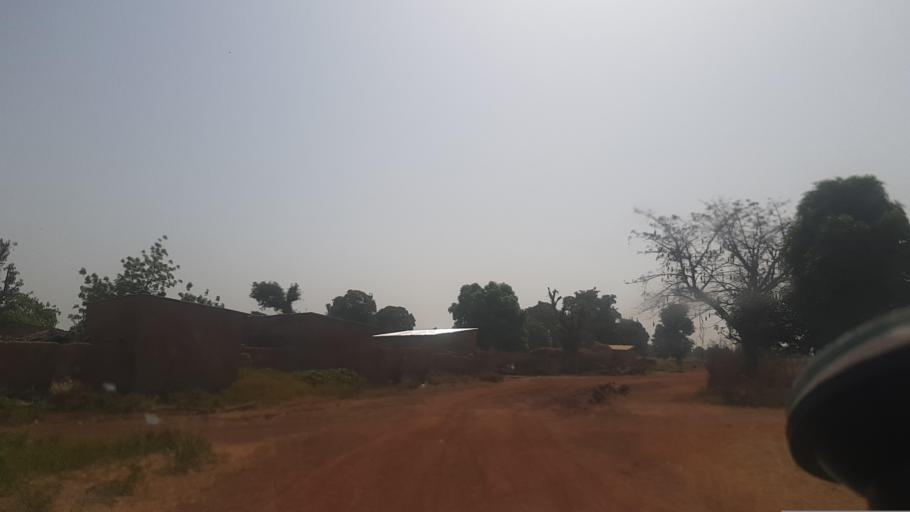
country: ML
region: Segou
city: Baroueli
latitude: 13.0097
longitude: -6.4218
